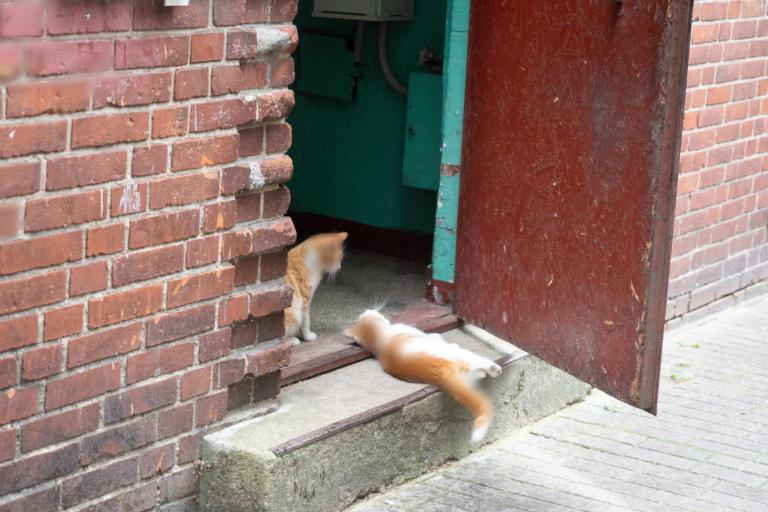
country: RU
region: Kaliningrad
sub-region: Gorod Kaliningrad
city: Kaliningrad
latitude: 54.7077
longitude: 20.5381
